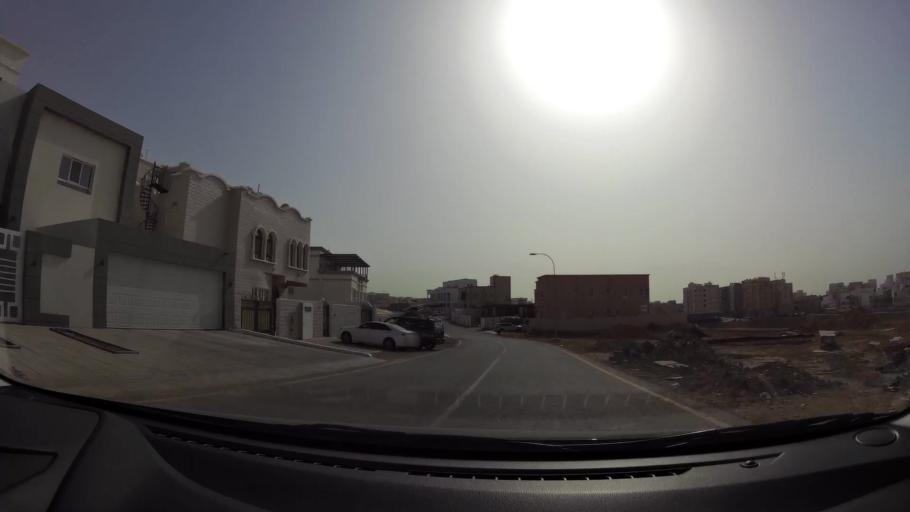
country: OM
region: Muhafazat Masqat
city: Bawshar
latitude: 23.5561
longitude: 58.3522
